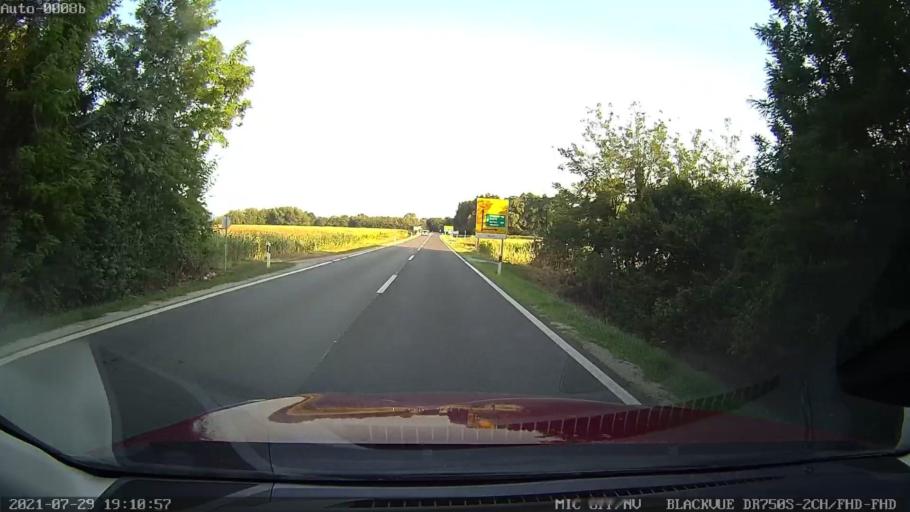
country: HR
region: Varazdinska
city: Jalzabet
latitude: 46.2839
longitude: 16.5057
